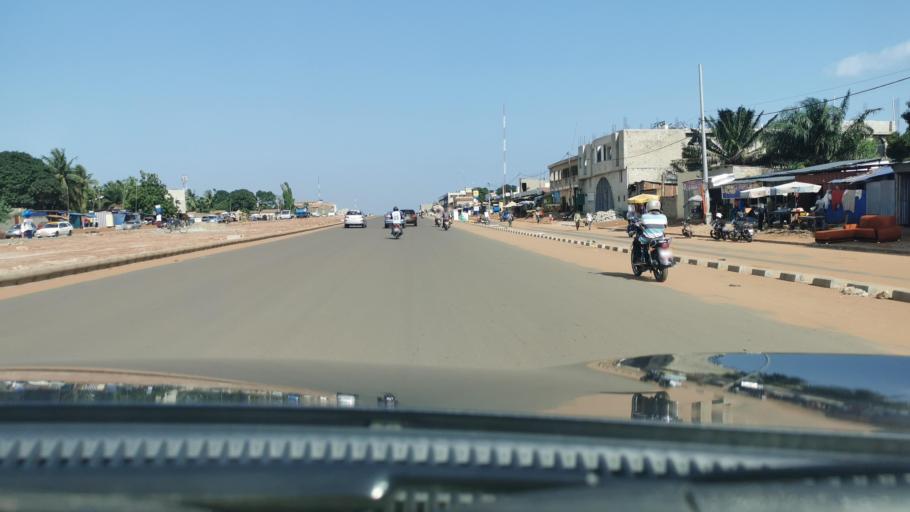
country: TG
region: Maritime
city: Lome
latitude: 6.2052
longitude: 1.1431
